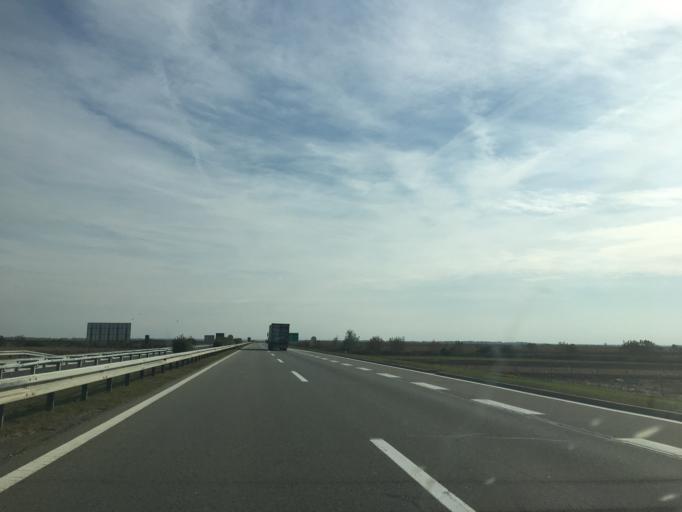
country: RS
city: Novi Karlovci
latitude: 45.0672
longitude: 20.1551
